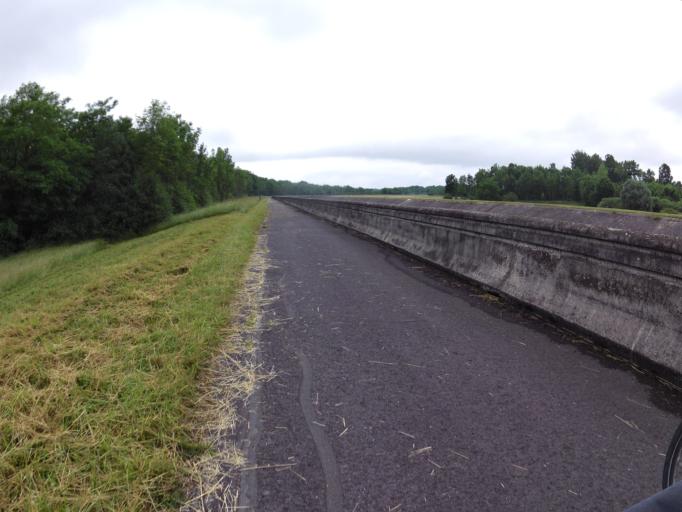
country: FR
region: Champagne-Ardenne
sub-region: Departement de la Haute-Marne
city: Villiers-en-Lieu
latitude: 48.6006
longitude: 4.8624
